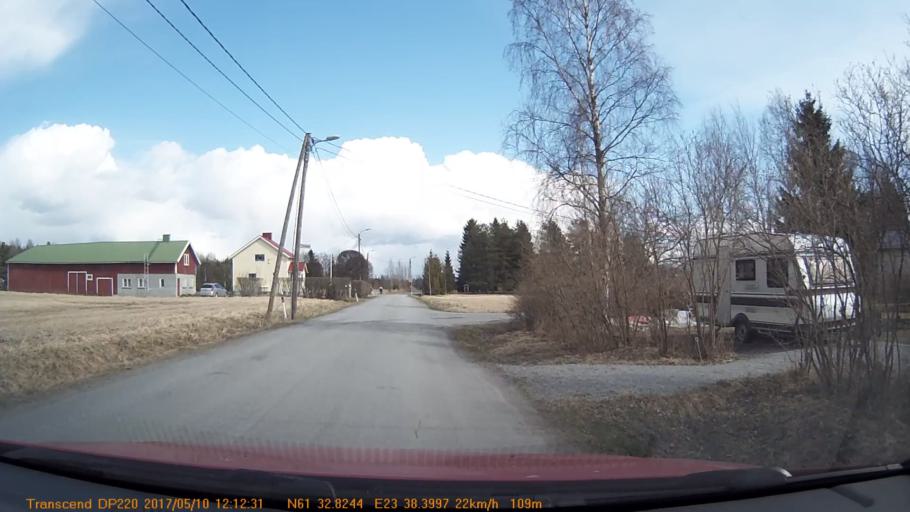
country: FI
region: Pirkanmaa
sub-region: Tampere
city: Yloejaervi
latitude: 61.5467
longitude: 23.6403
